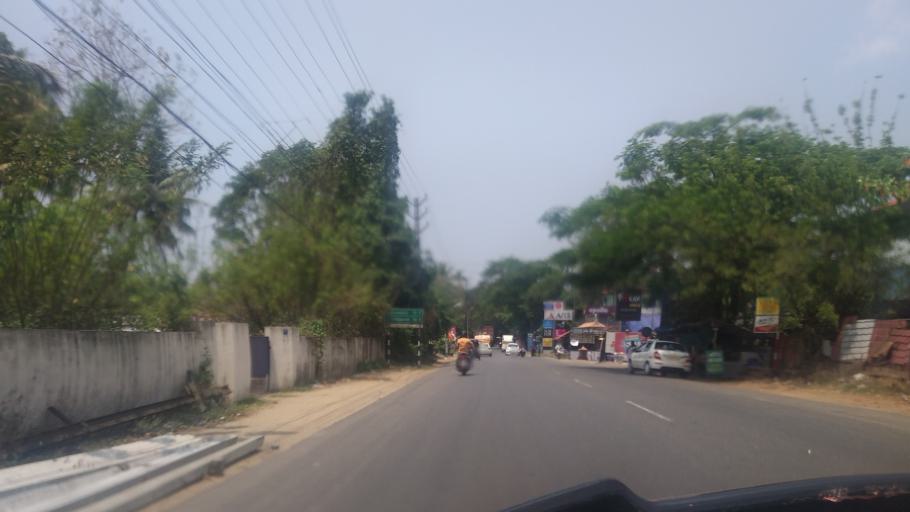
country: IN
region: Kerala
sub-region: Thrissur District
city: Kodungallur
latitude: 10.2353
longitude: 76.1942
